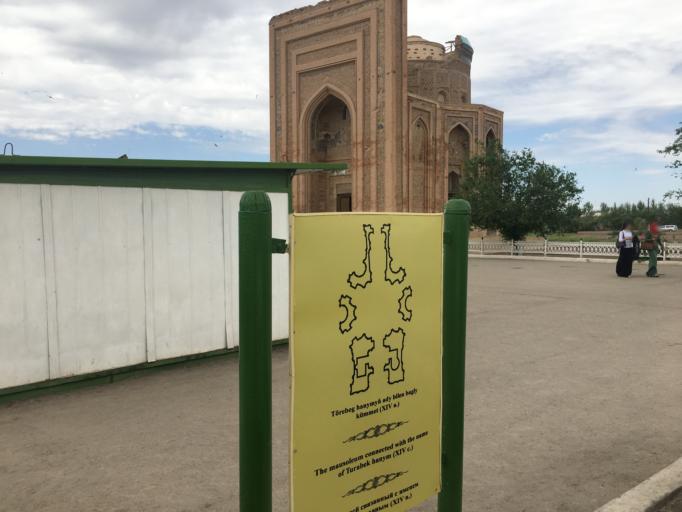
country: TM
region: Dasoguz
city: Koeneuergench
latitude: 42.3107
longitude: 59.1375
